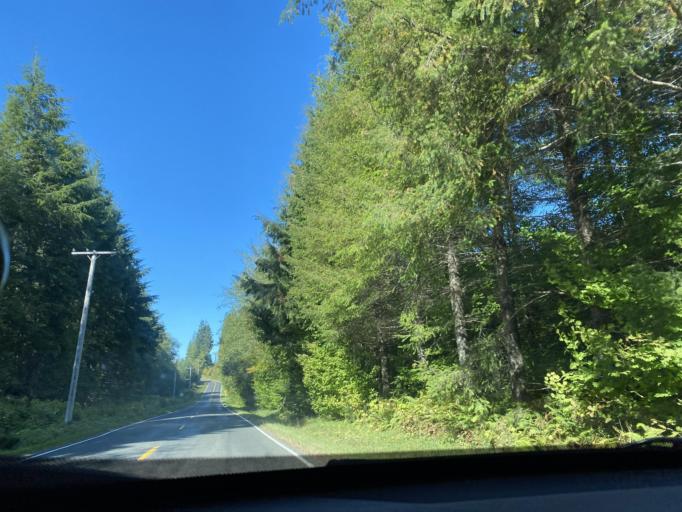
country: US
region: Washington
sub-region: Clallam County
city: Forks
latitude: 47.9479
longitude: -124.5020
